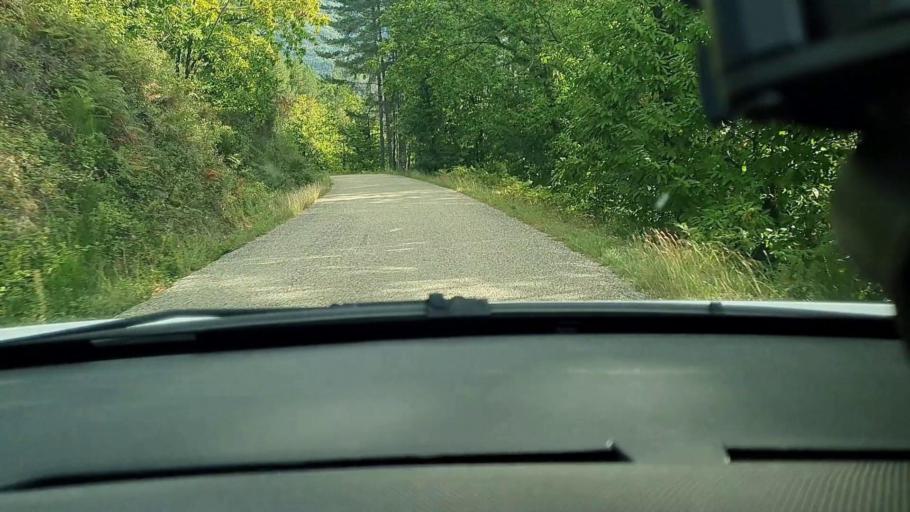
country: FR
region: Languedoc-Roussillon
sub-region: Departement du Gard
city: Besseges
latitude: 44.3520
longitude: 3.9832
